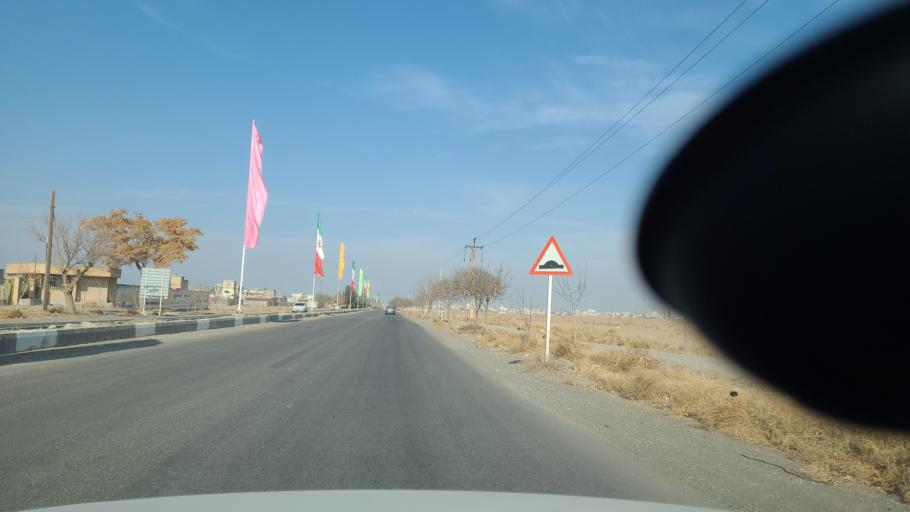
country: IR
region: Razavi Khorasan
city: Fariman
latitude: 35.6787
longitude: 59.8429
